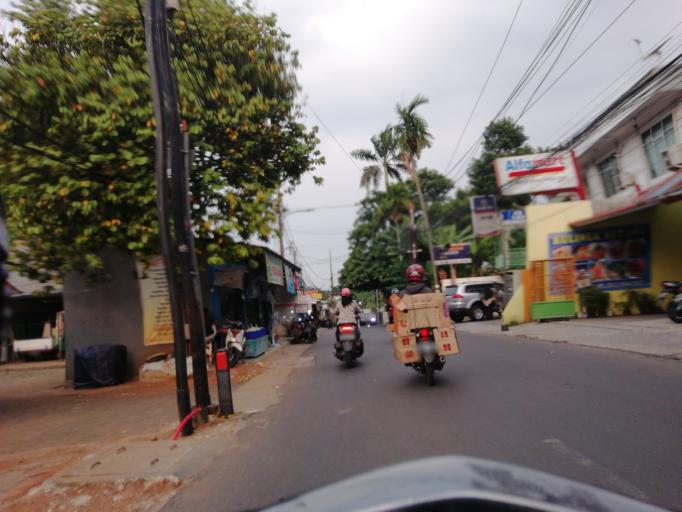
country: ID
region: West Java
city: Depok
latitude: -6.3273
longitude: 106.8164
